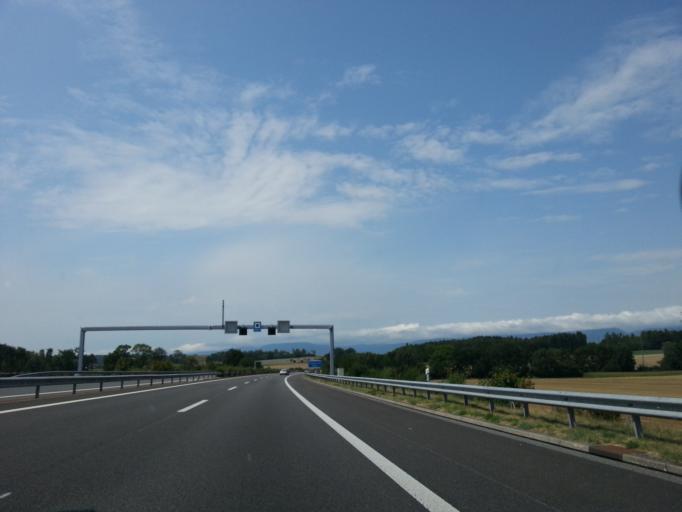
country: CH
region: Fribourg
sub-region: Broye District
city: Cugy
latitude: 46.8260
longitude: 6.8862
